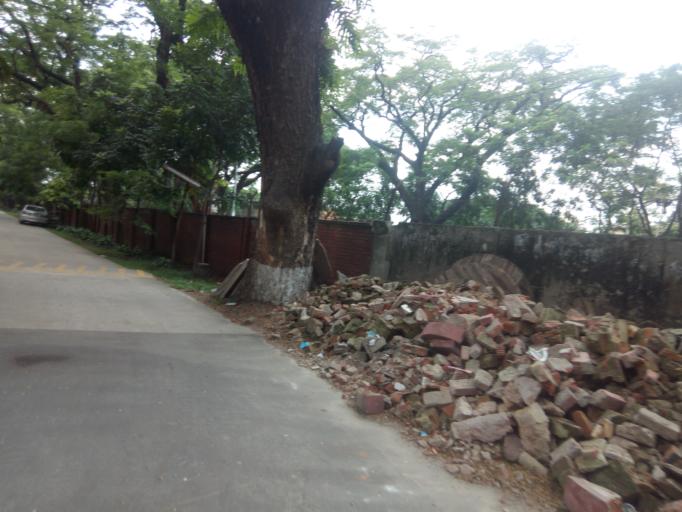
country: BD
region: Dhaka
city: Azimpur
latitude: 23.7280
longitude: 90.3916
